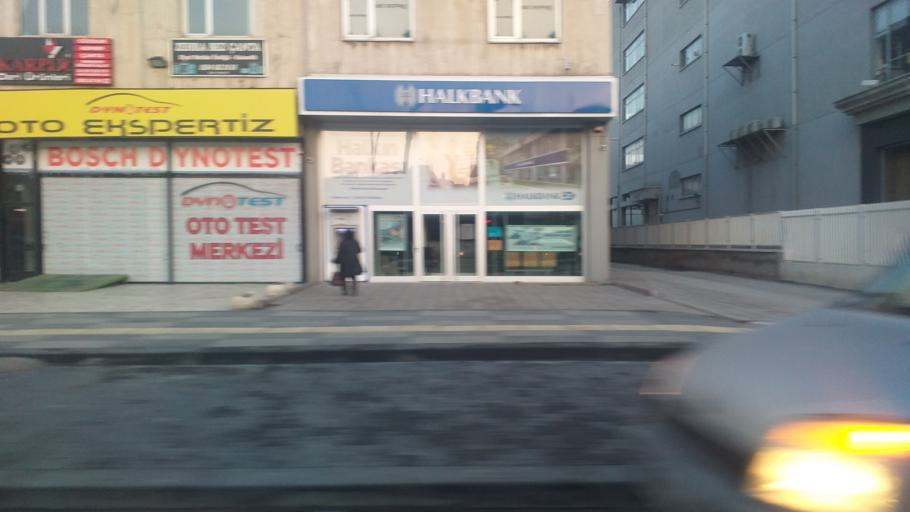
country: TR
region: Ankara
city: Ankara
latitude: 39.9504
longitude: 32.8529
